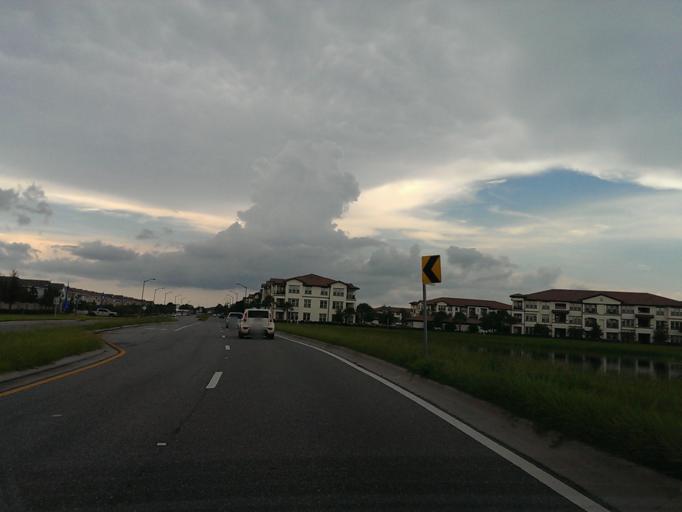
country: US
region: Florida
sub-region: Orange County
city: Bay Hill
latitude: 28.4399
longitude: -81.5581
